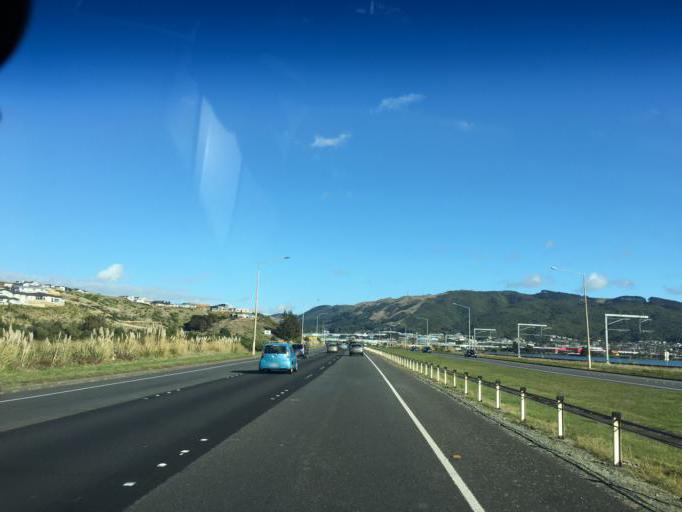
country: NZ
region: Wellington
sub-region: Porirua City
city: Porirua
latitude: -41.1237
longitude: 174.8504
